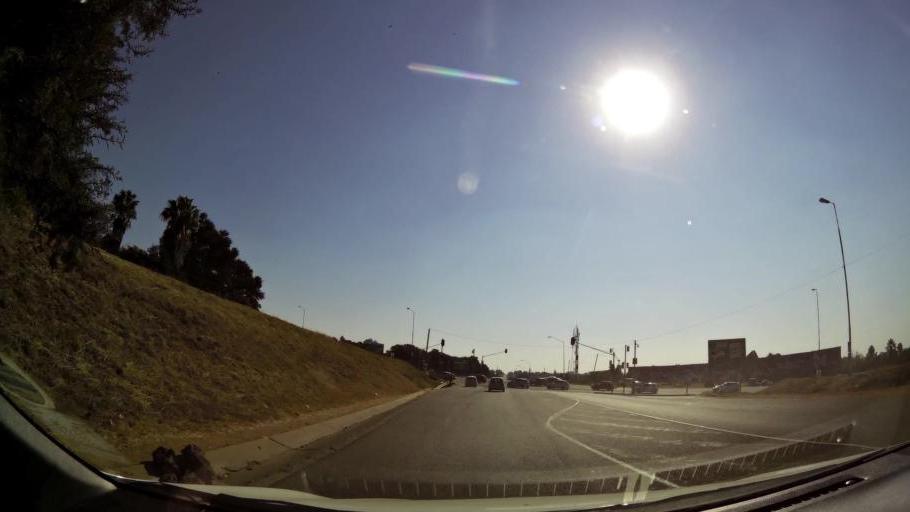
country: ZA
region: Gauteng
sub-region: City of Tshwane Metropolitan Municipality
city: Centurion
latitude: -25.8049
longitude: 28.2965
